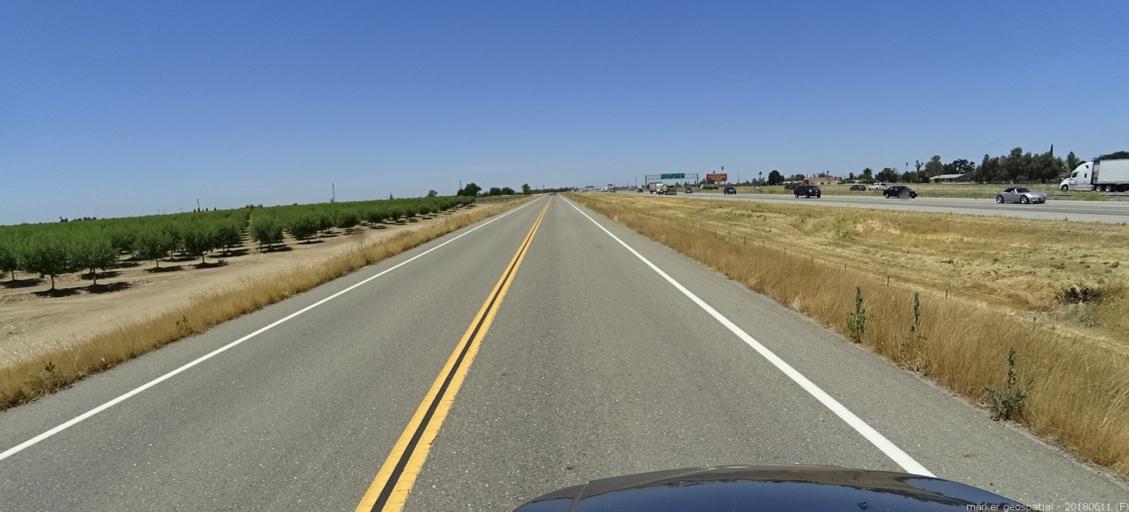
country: US
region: California
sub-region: Madera County
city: Fairmead
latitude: 37.0717
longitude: -120.1947
